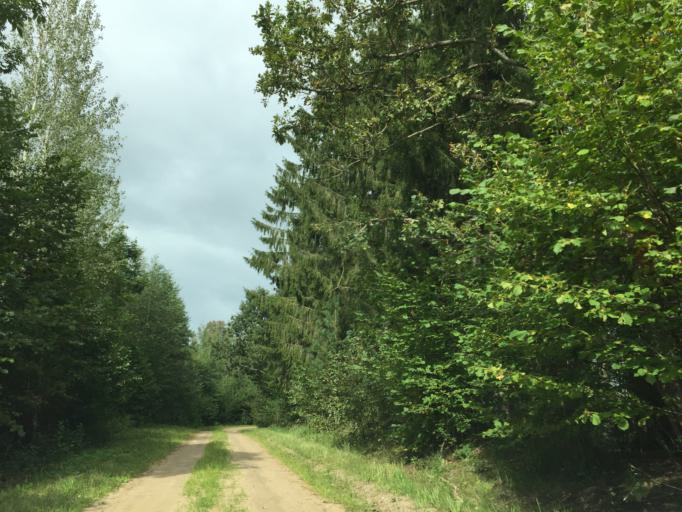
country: LV
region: Pargaujas
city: Stalbe
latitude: 57.5009
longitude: 24.9186
